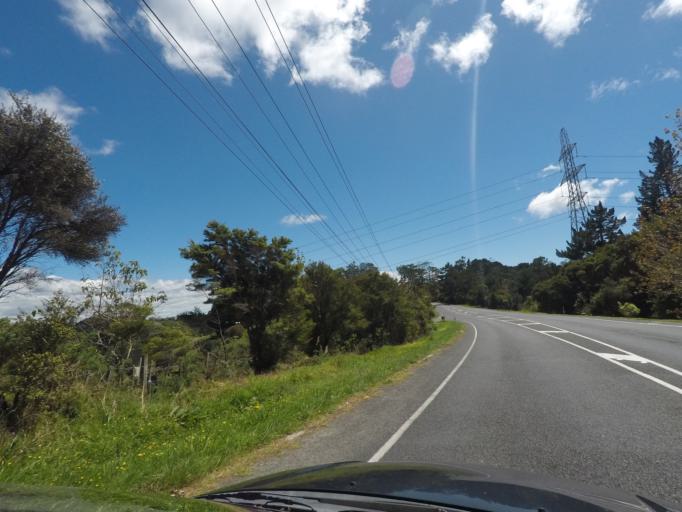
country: NZ
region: Auckland
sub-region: Auckland
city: Rothesay Bay
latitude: -36.7364
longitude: 174.6759
